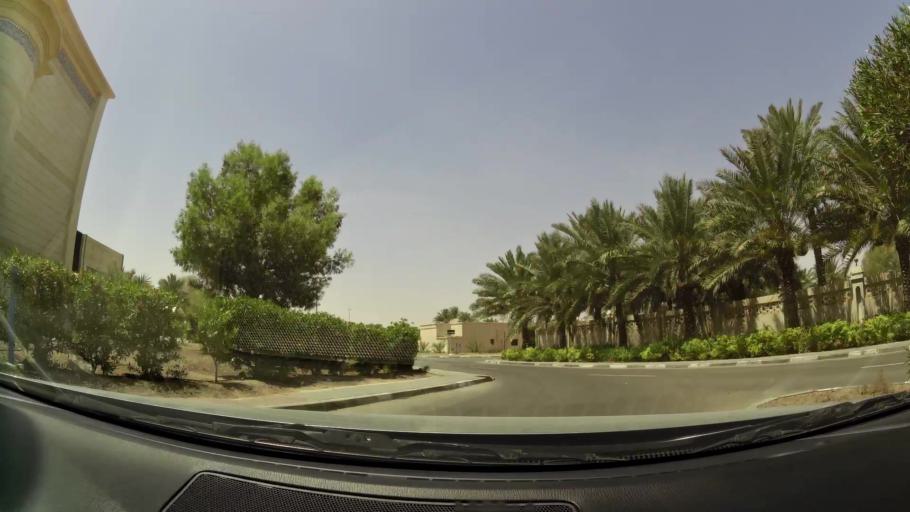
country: OM
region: Al Buraimi
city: Al Buraymi
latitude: 24.2731
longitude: 55.7555
